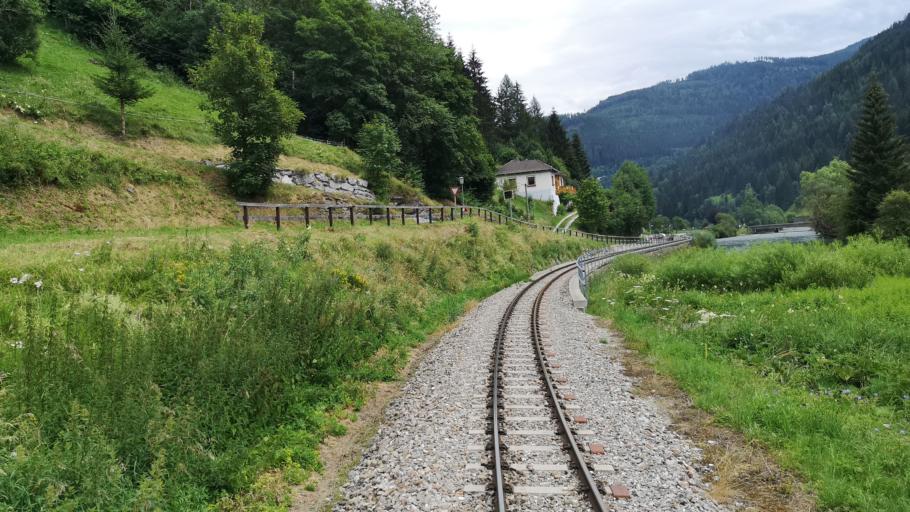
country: AT
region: Salzburg
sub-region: Politischer Bezirk Tamsweg
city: Ramingstein
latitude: 47.0781
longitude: 13.8180
